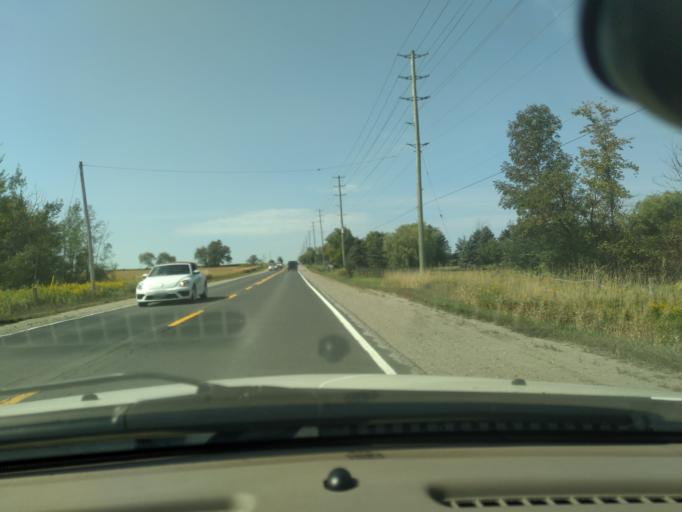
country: CA
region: Ontario
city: Innisfil
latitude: 44.2819
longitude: -79.6940
